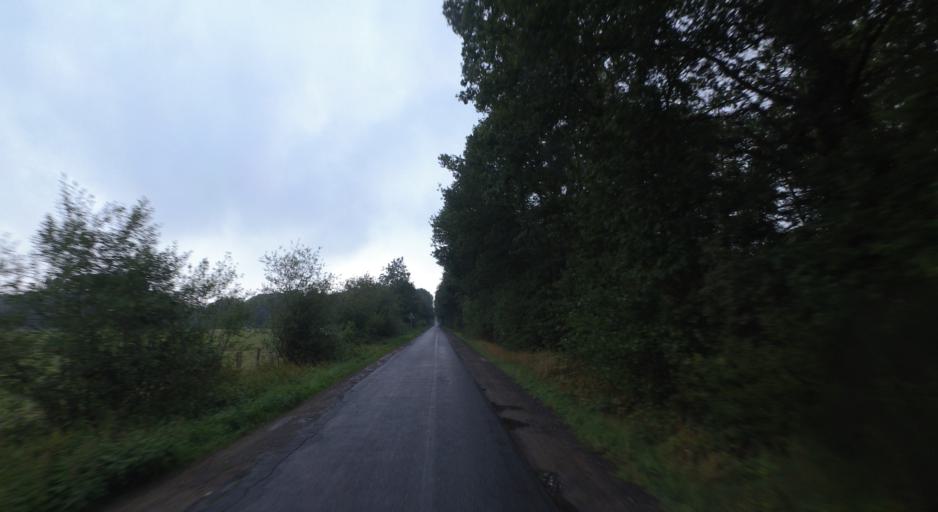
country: DE
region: North Rhine-Westphalia
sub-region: Regierungsbezirk Dusseldorf
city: Wesel
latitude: 51.7013
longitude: 6.6270
